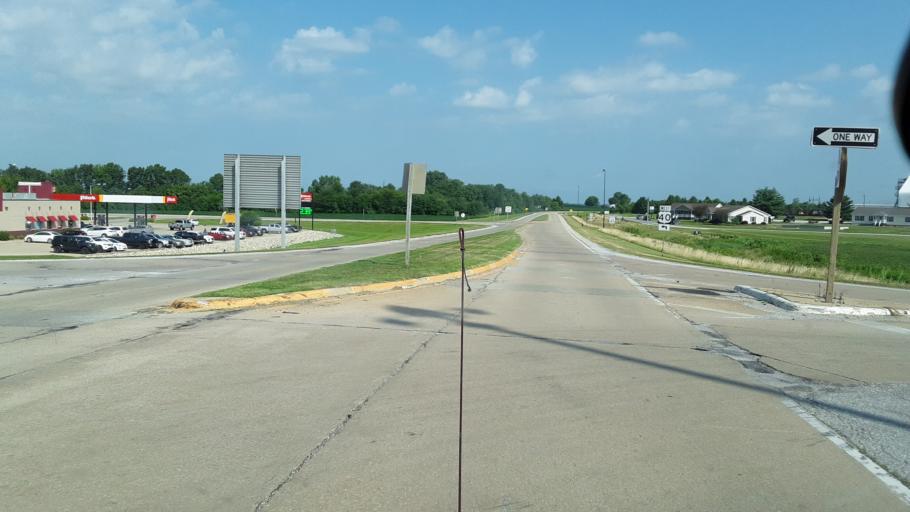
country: US
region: Illinois
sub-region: Fayette County
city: Vandalia
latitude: 38.9708
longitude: -89.1343
